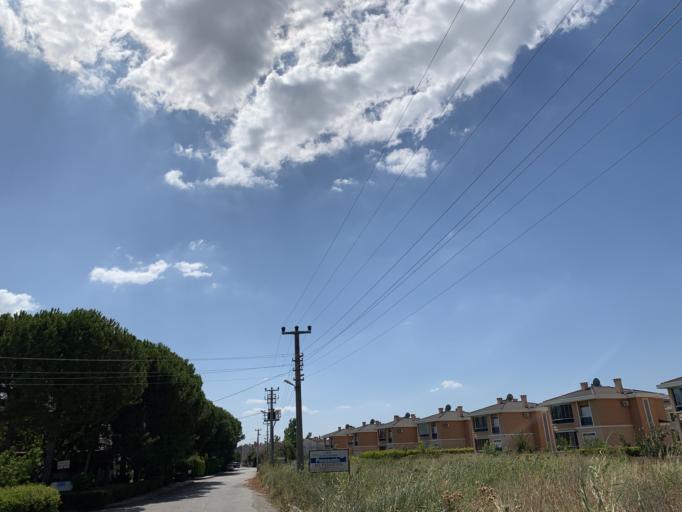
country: TR
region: Balikesir
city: Altinoluk
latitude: 39.5627
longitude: 26.8377
